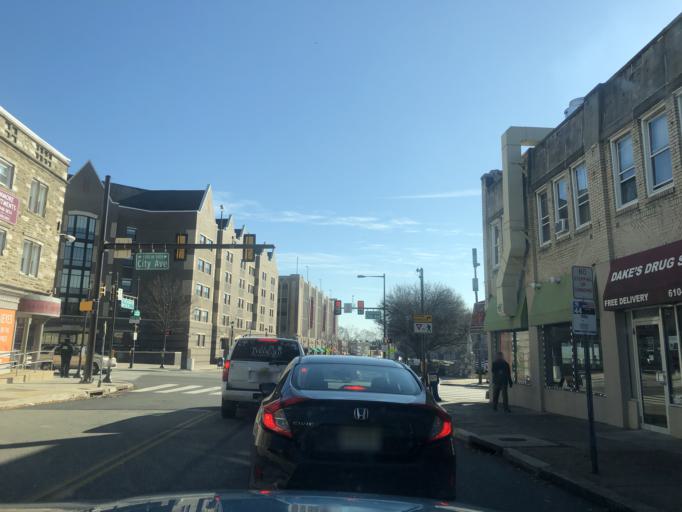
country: US
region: Pennsylvania
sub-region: Montgomery County
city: Bala-Cynwyd
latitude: 39.9973
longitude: -75.2356
